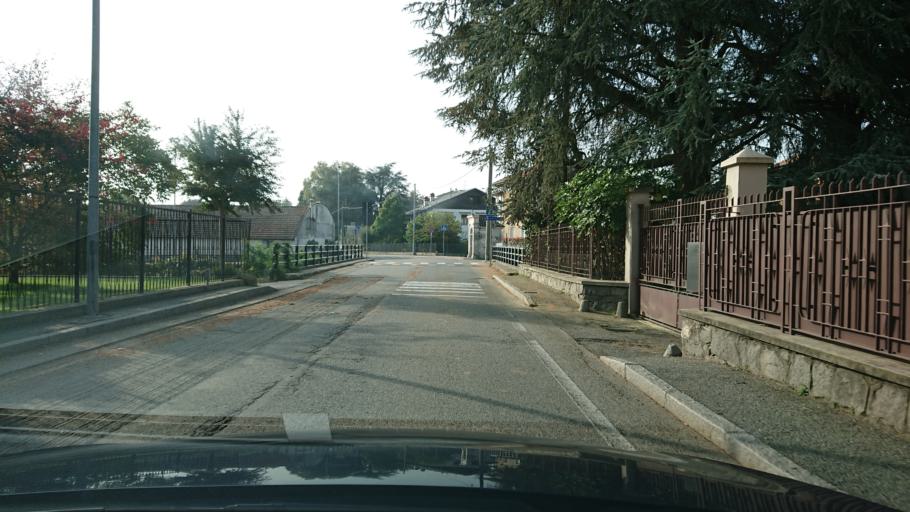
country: IT
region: Piedmont
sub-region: Provincia di Biella
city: Vigliano Biellese
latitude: 45.5668
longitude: 8.1077
